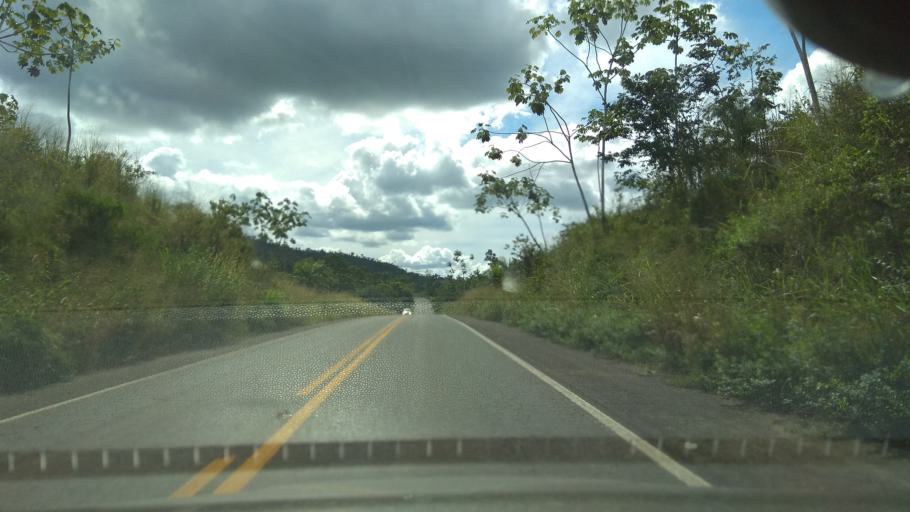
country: BR
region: Bahia
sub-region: Ubaitaba
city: Ubaitaba
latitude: -14.2509
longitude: -39.3568
